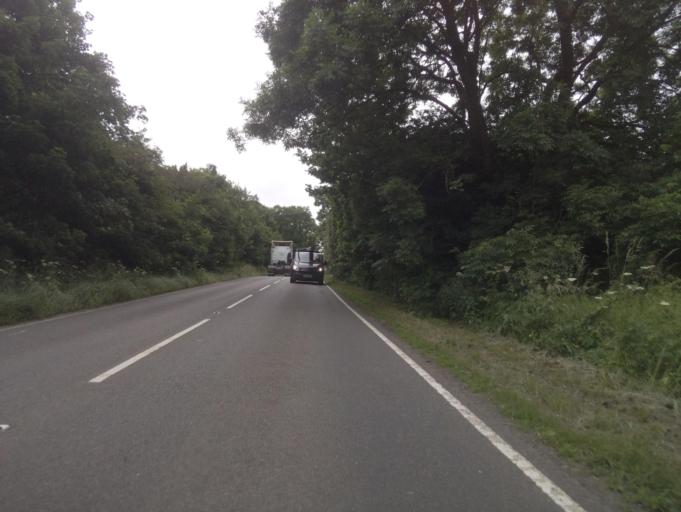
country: GB
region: England
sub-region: Leicestershire
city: Sileby
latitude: 52.8060
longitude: -1.0701
